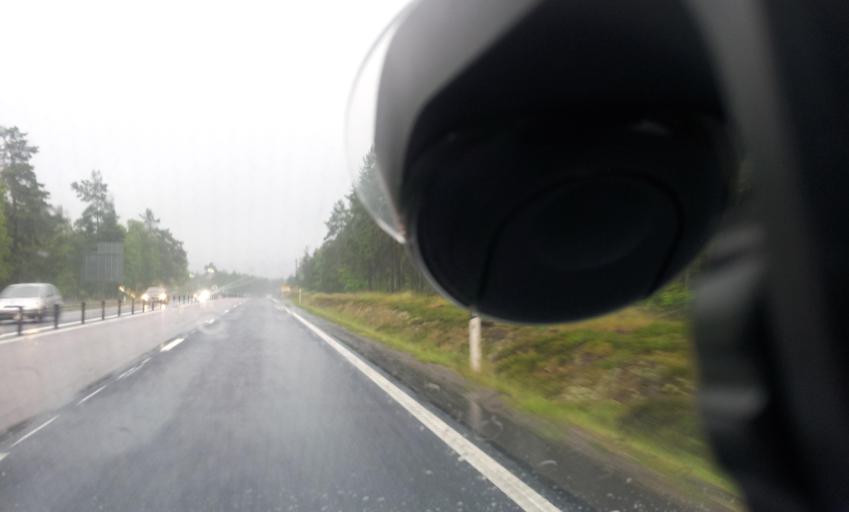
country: SE
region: Kalmar
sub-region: Oskarshamns Kommun
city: Oskarshamn
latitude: 57.3663
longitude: 16.4933
